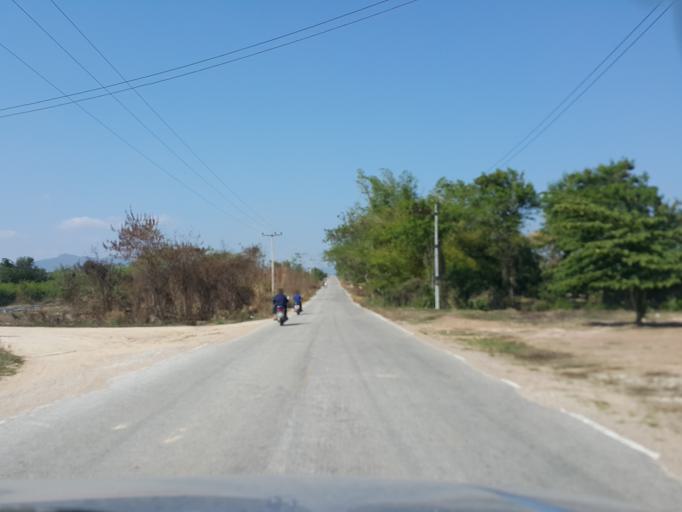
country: TH
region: Chiang Mai
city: Mae Wang
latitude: 18.5545
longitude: 98.7956
